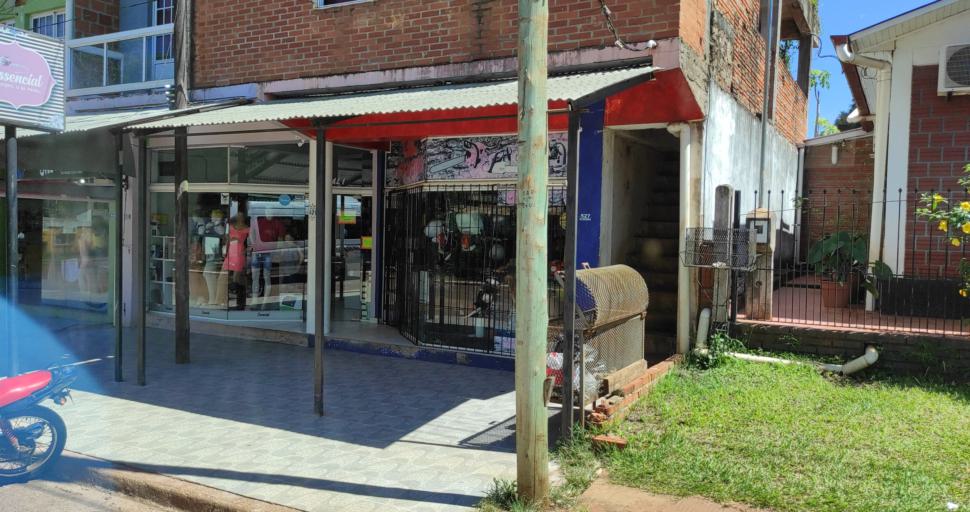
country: AR
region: Misiones
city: El Soberbio
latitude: -27.2959
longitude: -54.1994
